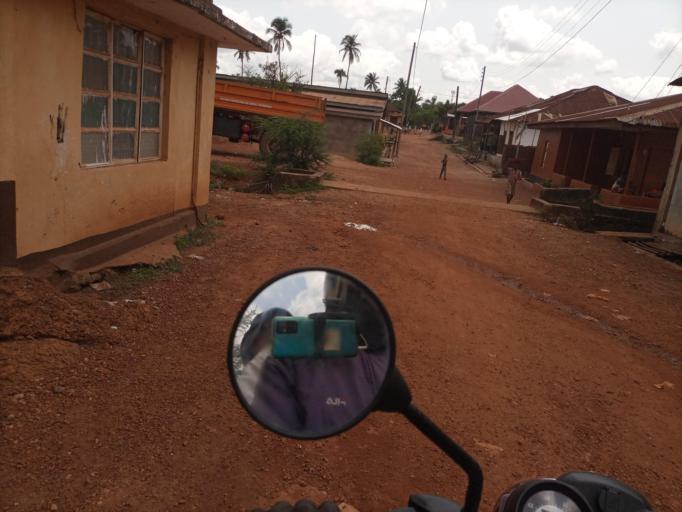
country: SL
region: Southern Province
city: Bo
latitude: 7.9563
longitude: -11.7350
